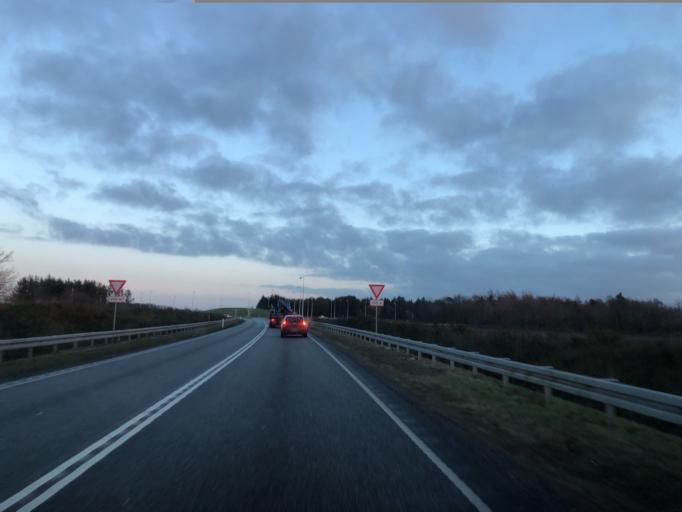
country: DK
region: Central Jutland
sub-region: Herning Kommune
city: Sunds
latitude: 56.1889
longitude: 9.0126
